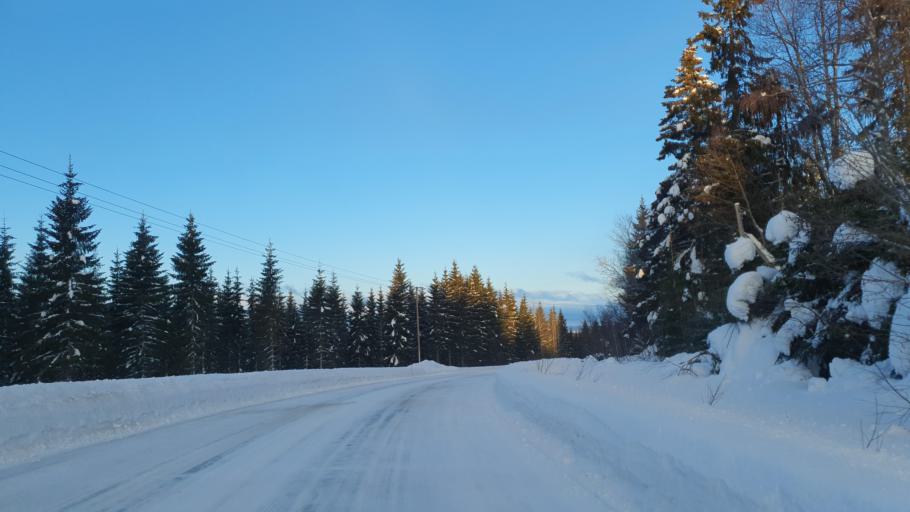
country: FI
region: Kainuu
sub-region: Kajaani
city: Ristijaervi
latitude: 64.3377
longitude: 28.0627
